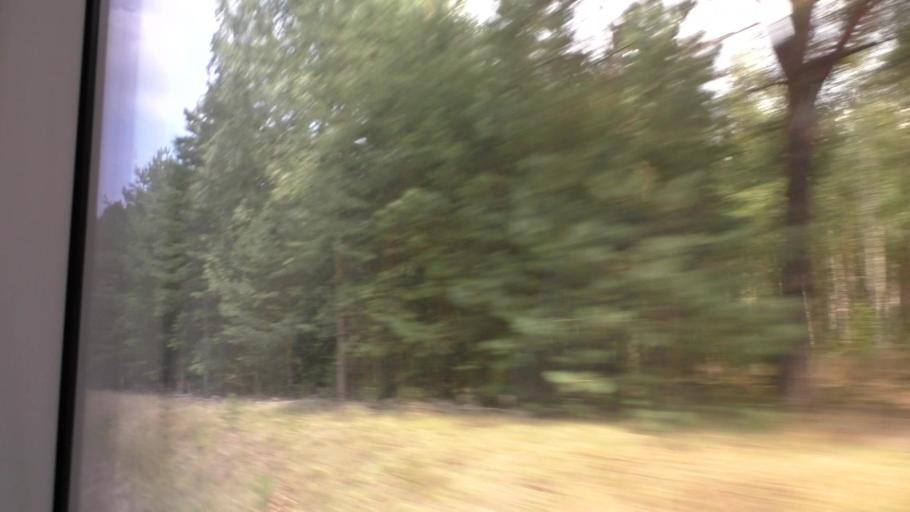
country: DE
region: Brandenburg
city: Mixdorf
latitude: 52.1785
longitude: 14.3831
